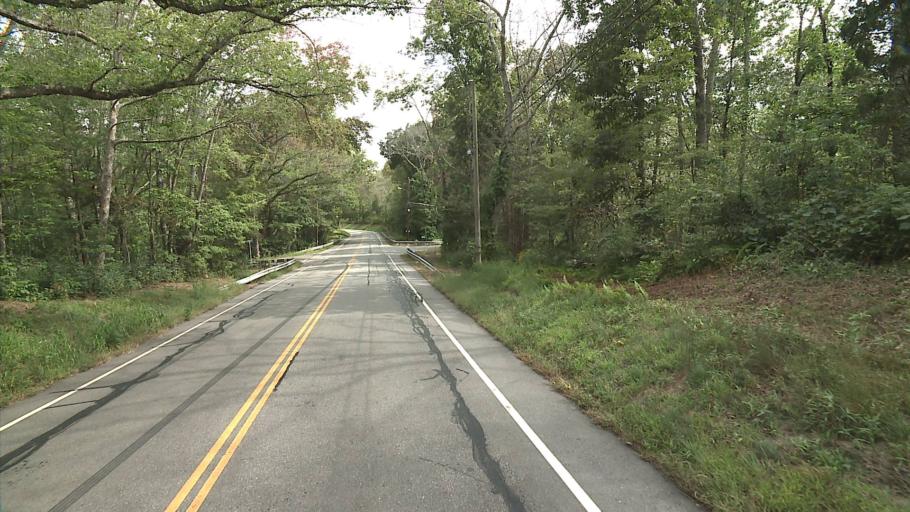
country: US
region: Connecticut
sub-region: New London County
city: Jewett City
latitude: 41.6516
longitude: -71.9746
